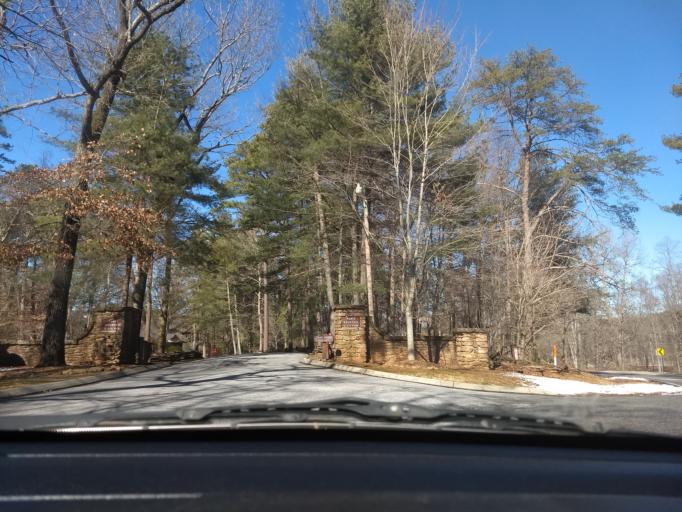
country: US
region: South Carolina
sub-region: Greenville County
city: Wade Hampton
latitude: 34.9253
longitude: -82.3654
